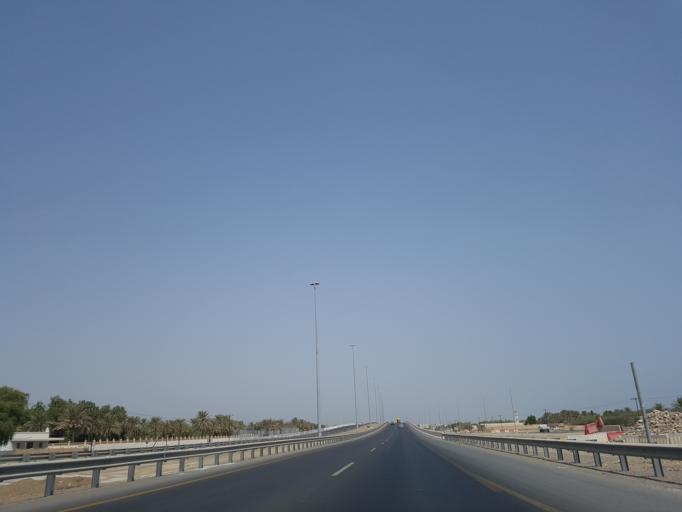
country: OM
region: Al Batinah
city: Saham
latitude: 24.1007
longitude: 56.9213
